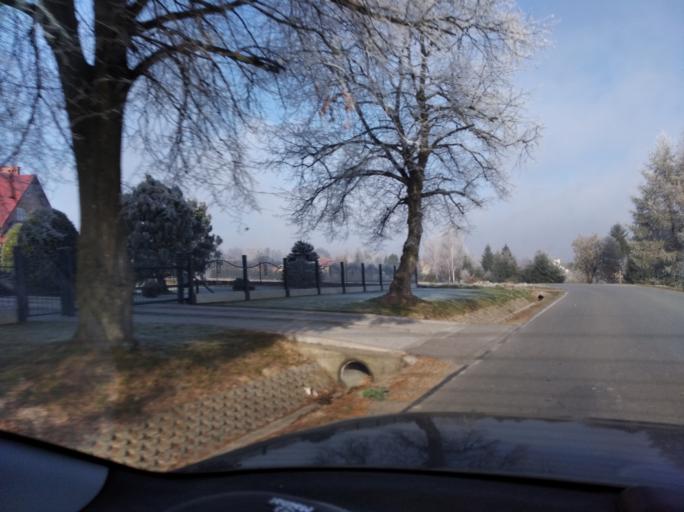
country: PL
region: Subcarpathian Voivodeship
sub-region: Powiat strzyzowski
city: Wysoka Strzyzowska
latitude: 49.8433
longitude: 21.7328
